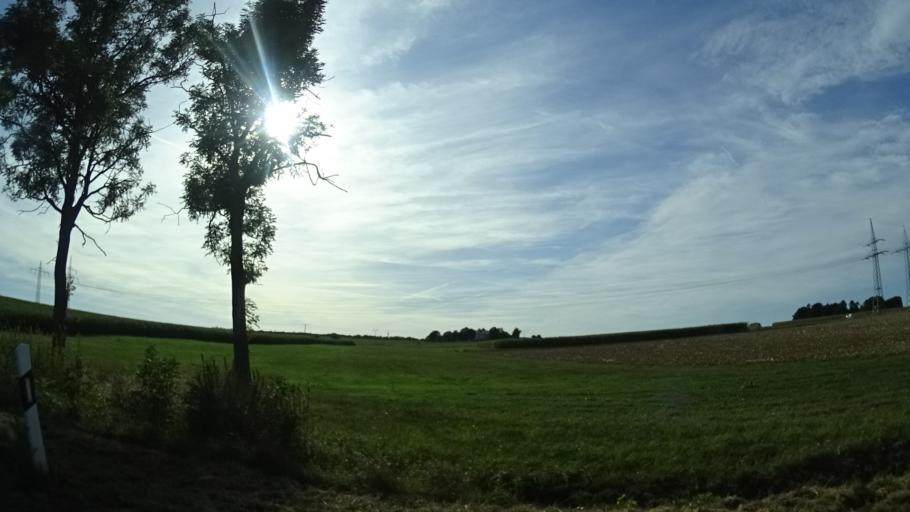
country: DE
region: Hesse
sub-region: Regierungsbezirk Kassel
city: Kunzell
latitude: 50.5352
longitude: 9.7508
